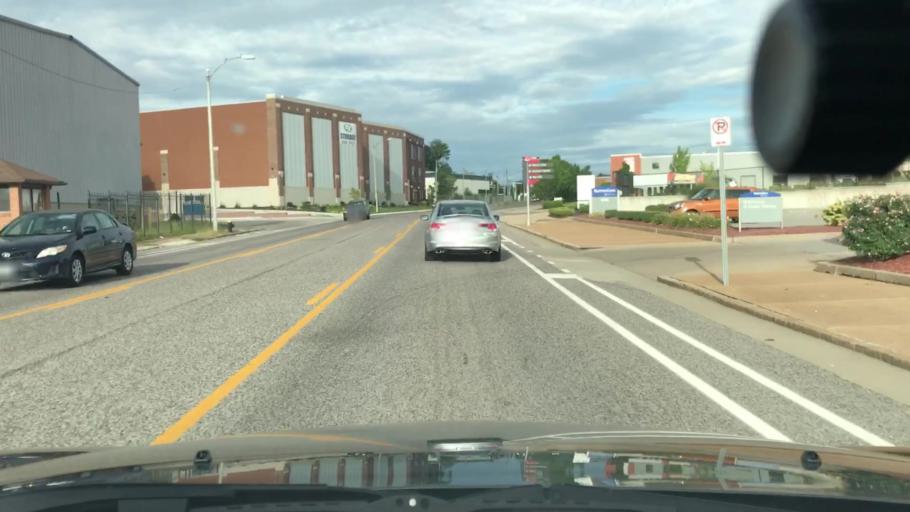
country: US
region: Missouri
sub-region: Saint Louis County
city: University City
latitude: 38.6252
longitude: -90.2689
